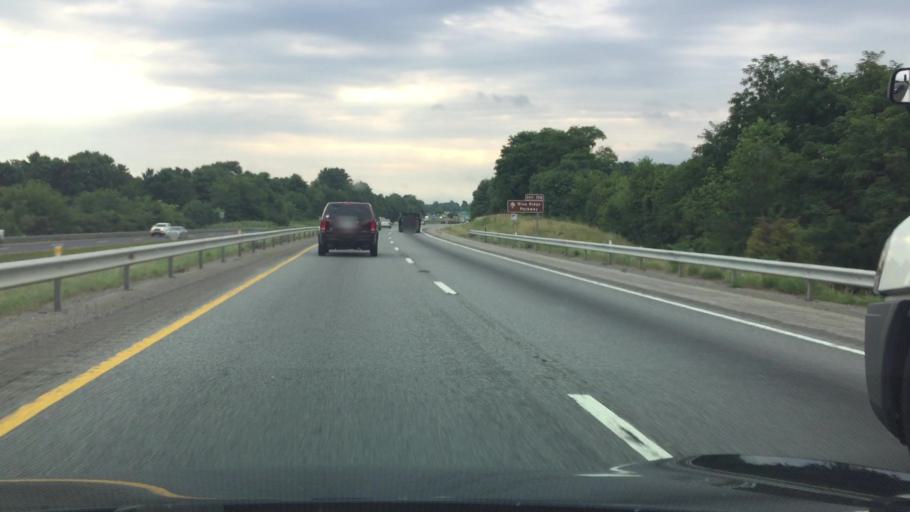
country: US
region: Virginia
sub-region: Montgomery County
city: Christiansburg
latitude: 37.1153
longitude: -80.4370
